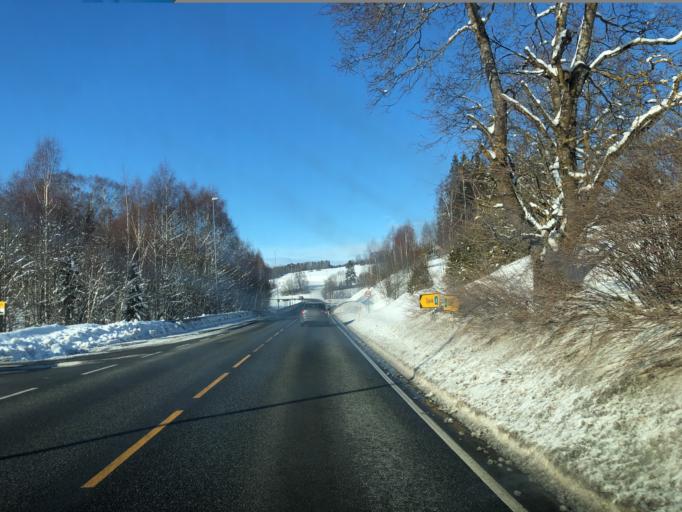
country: NO
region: Oppland
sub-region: Lunner
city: Roa
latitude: 60.3094
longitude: 10.5957
